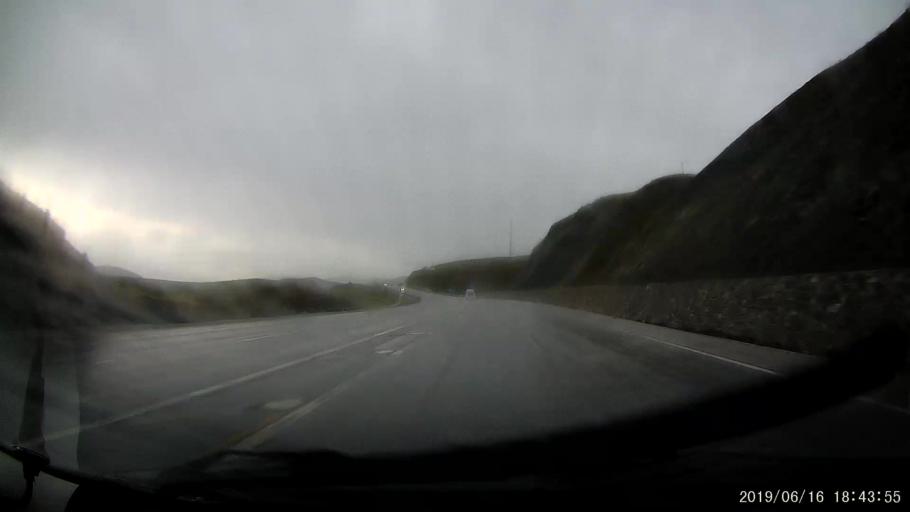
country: TR
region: Erzincan
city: Doganbeyli
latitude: 39.8713
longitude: 39.0832
